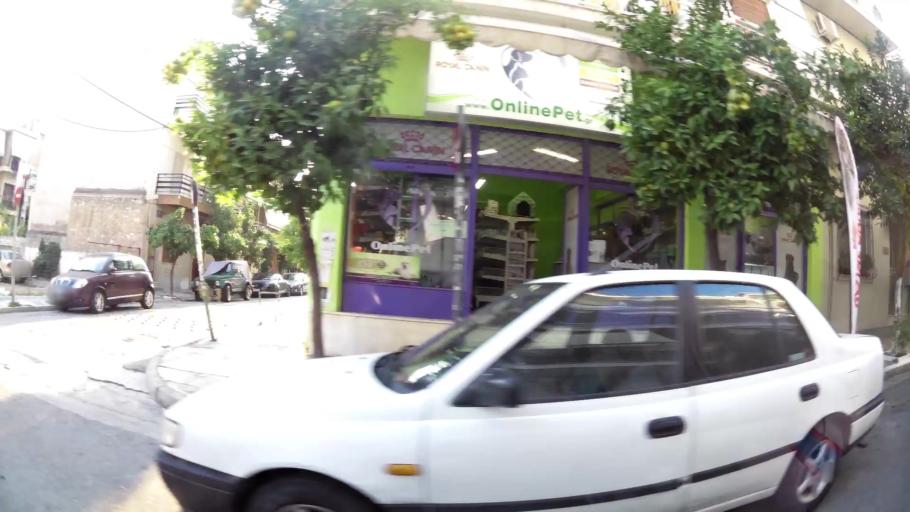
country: GR
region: Attica
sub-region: Nomos Piraios
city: Korydallos
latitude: 37.9758
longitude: 23.6449
